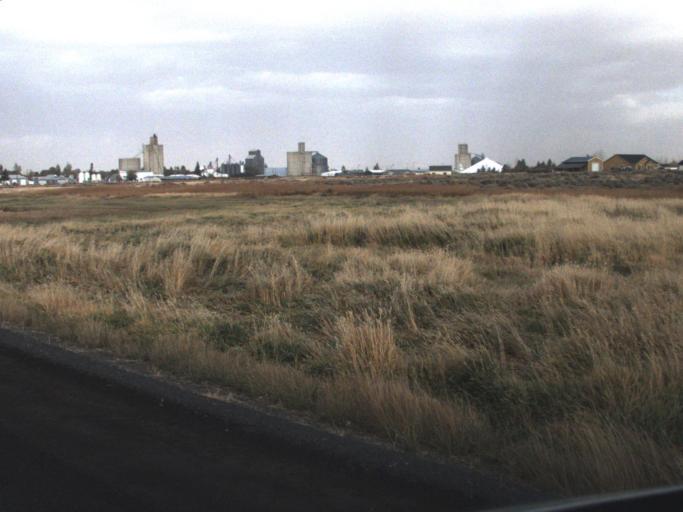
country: US
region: Washington
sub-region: Lincoln County
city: Davenport
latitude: 47.6388
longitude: -118.1625
